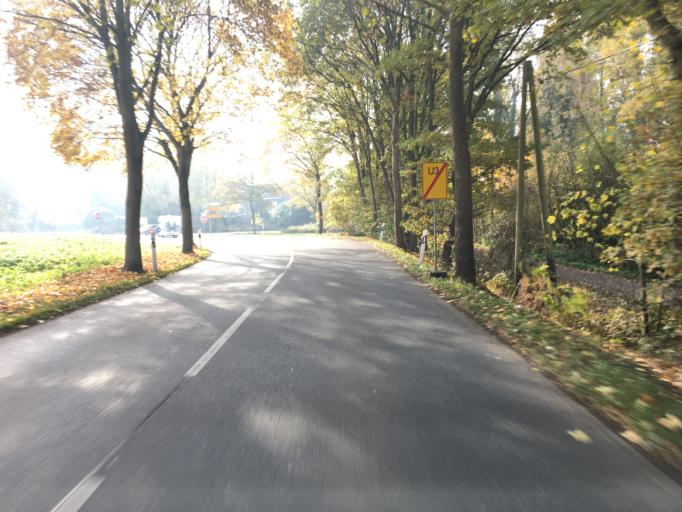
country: DE
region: North Rhine-Westphalia
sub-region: Regierungsbezirk Dusseldorf
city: Xanten
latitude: 51.6446
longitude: 6.4275
